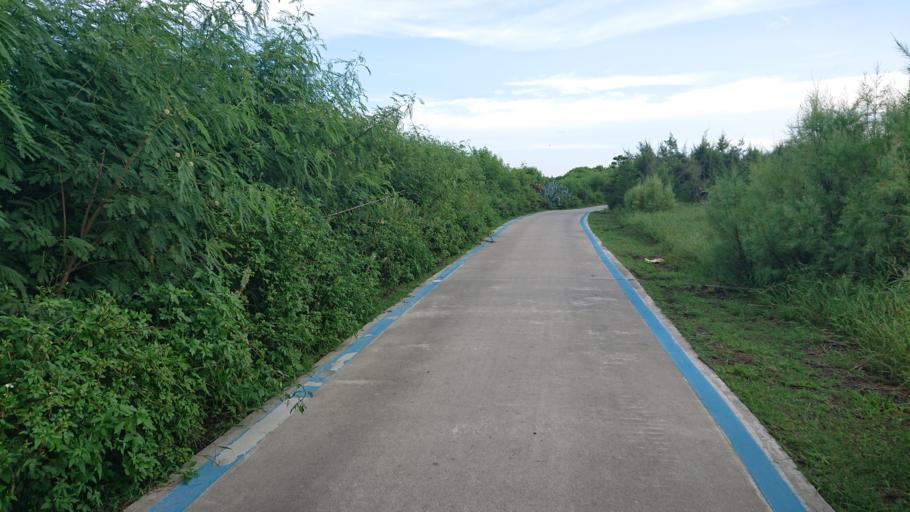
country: TW
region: Taiwan
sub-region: Penghu
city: Ma-kung
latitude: 23.5205
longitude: 119.6107
